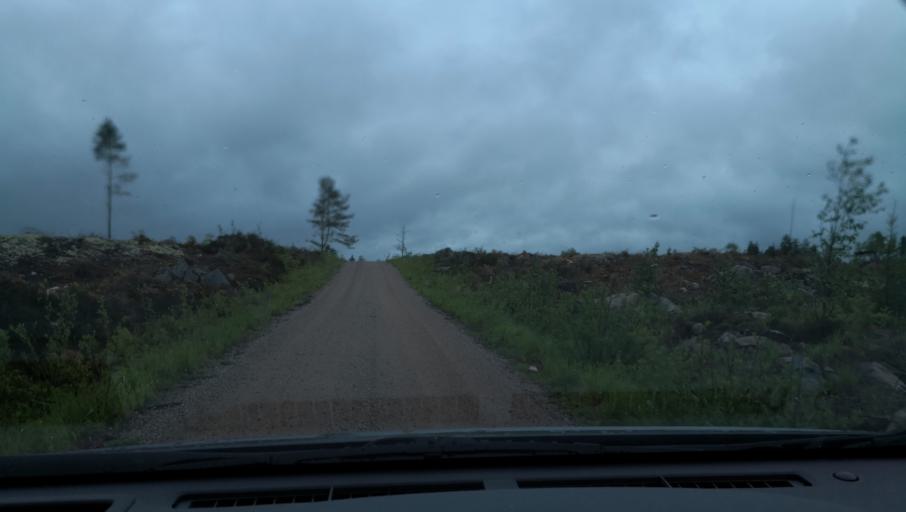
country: SE
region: Uppsala
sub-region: Enkopings Kommun
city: Orsundsbro
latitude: 59.9384
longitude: 17.3125
